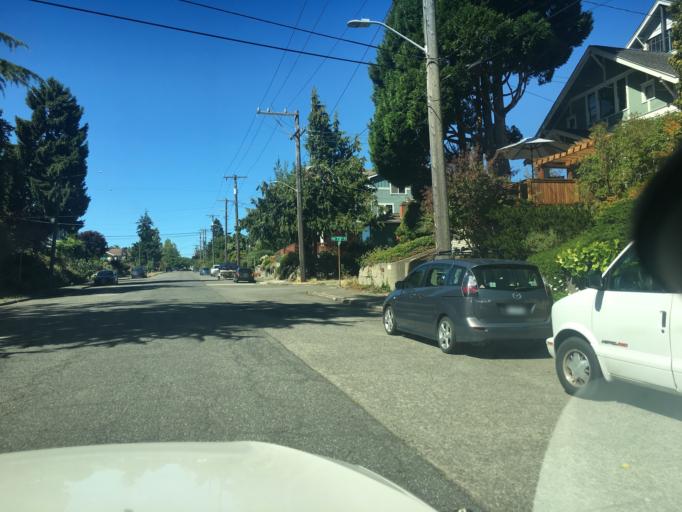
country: US
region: Washington
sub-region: King County
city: Shoreline
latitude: 47.6809
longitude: -122.3930
